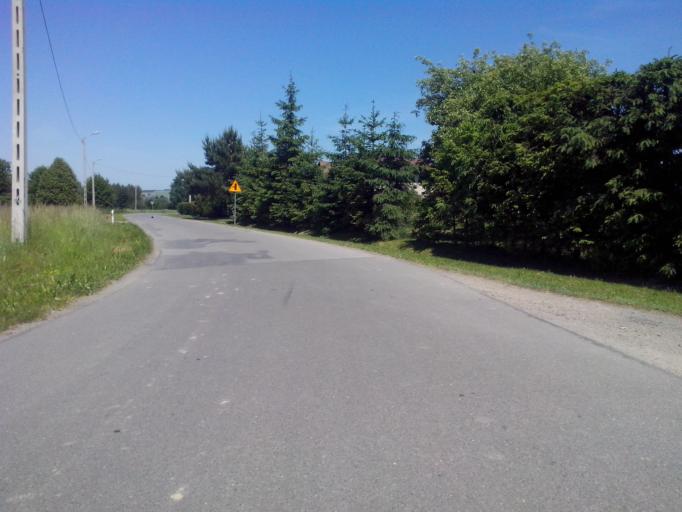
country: PL
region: Subcarpathian Voivodeship
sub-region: Powiat strzyzowski
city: Wisniowa
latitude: 49.8568
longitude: 21.6871
